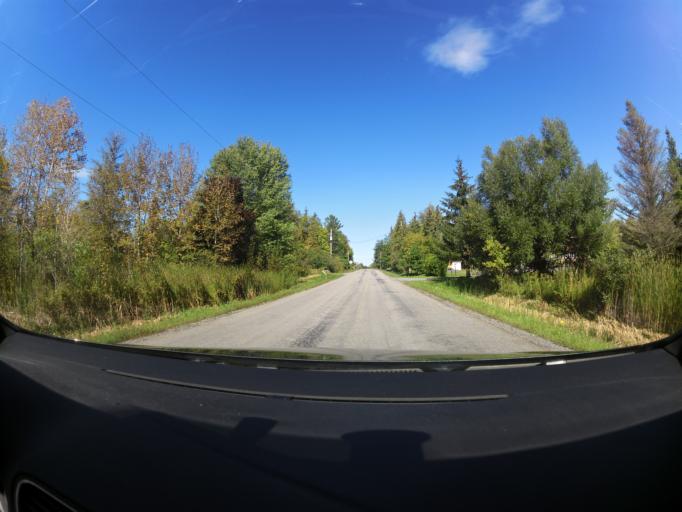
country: CA
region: Ontario
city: Bells Corners
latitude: 45.2650
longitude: -75.9600
